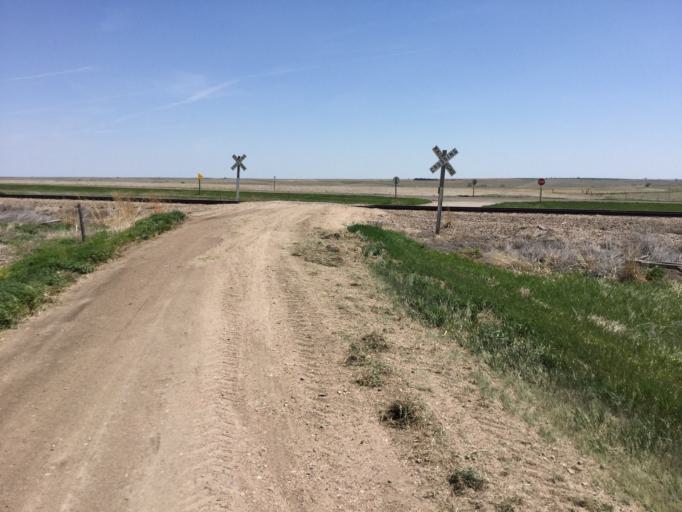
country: US
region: Kansas
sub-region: Decatur County
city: Oberlin
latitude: 39.6344
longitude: -100.3857
